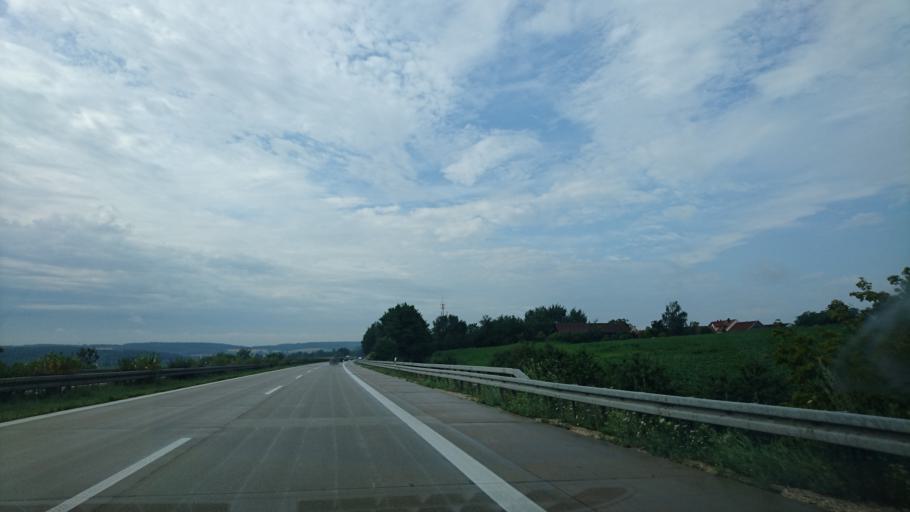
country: DE
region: Bavaria
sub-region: Lower Bavaria
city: Bad Abbach
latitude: 48.9431
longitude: 12.0916
